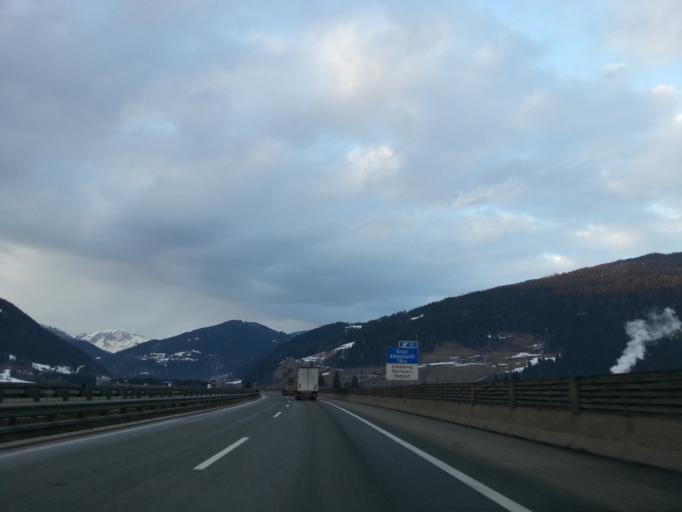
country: AT
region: Salzburg
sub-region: Politischer Bezirk Sankt Johann im Pongau
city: Altenmarkt im Pongau
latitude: 47.3819
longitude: 13.4017
